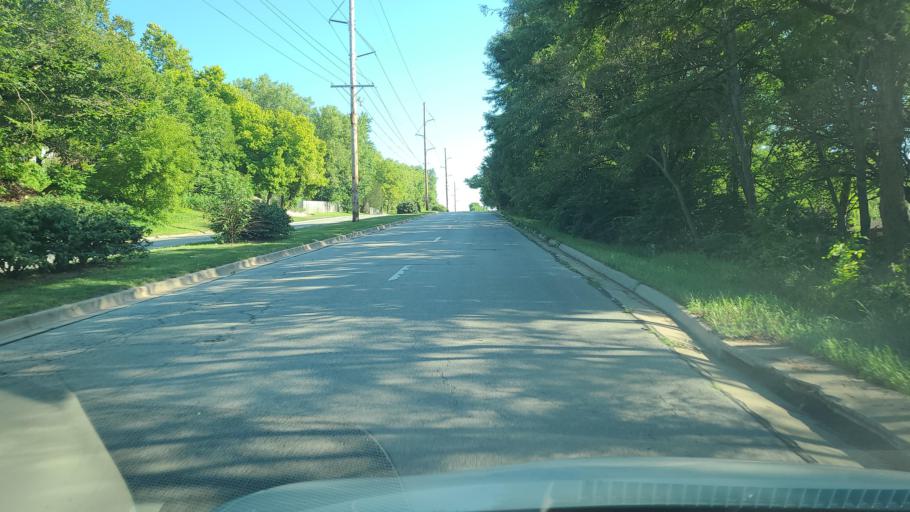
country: US
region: Kansas
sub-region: Douglas County
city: Lawrence
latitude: 38.9802
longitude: -95.2792
